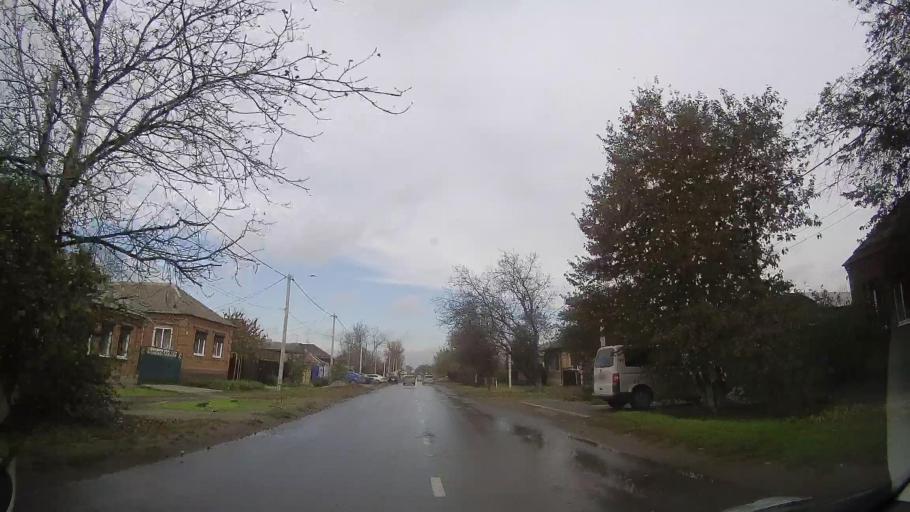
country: RU
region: Rostov
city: Bataysk
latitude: 47.1316
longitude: 39.7679
